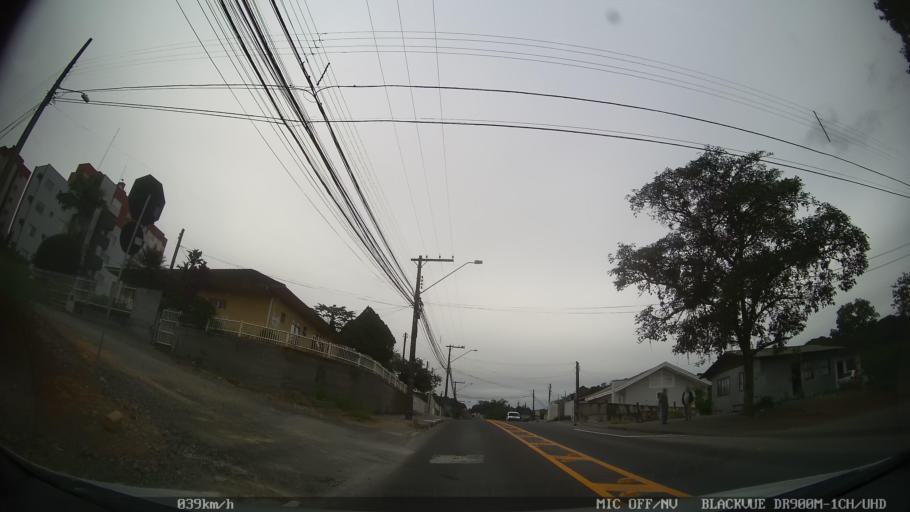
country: BR
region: Santa Catarina
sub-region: Joinville
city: Joinville
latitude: -26.2596
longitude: -48.8483
